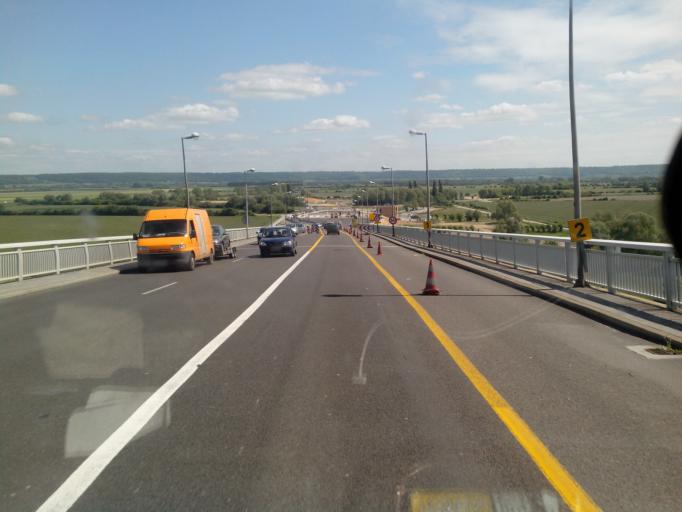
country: FR
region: Haute-Normandie
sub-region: Departement de la Seine-Maritime
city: Tancarville
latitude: 49.4674
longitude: 0.4702
